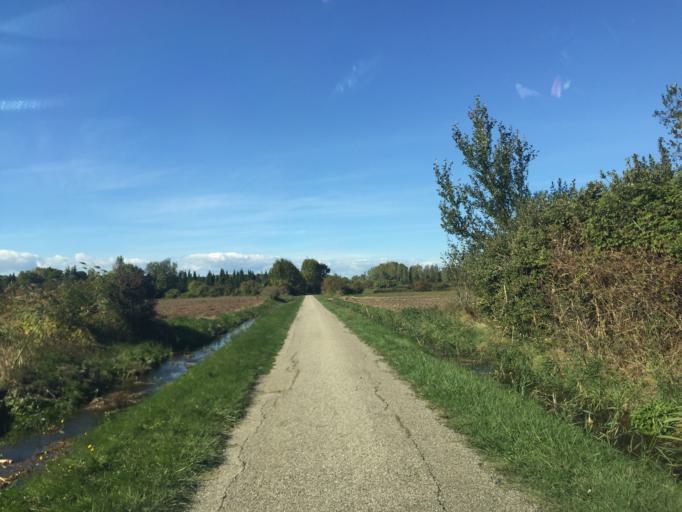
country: FR
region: Provence-Alpes-Cote d'Azur
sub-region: Departement du Vaucluse
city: Courthezon
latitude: 44.0840
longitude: 4.8684
